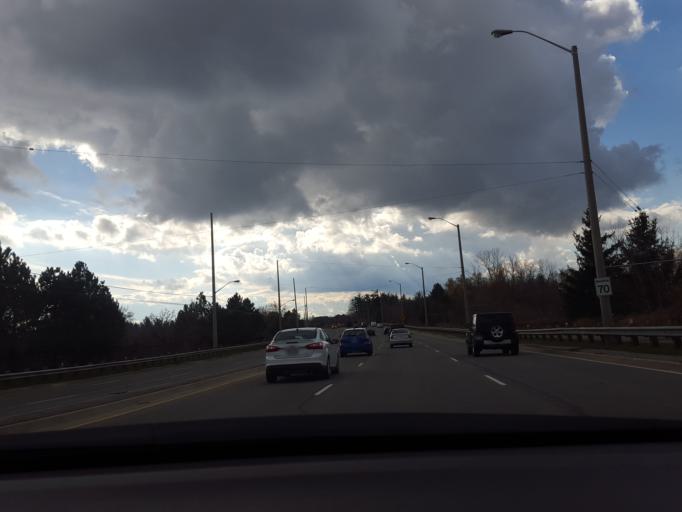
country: CA
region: Ontario
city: Brampton
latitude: 43.6318
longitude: -79.7373
